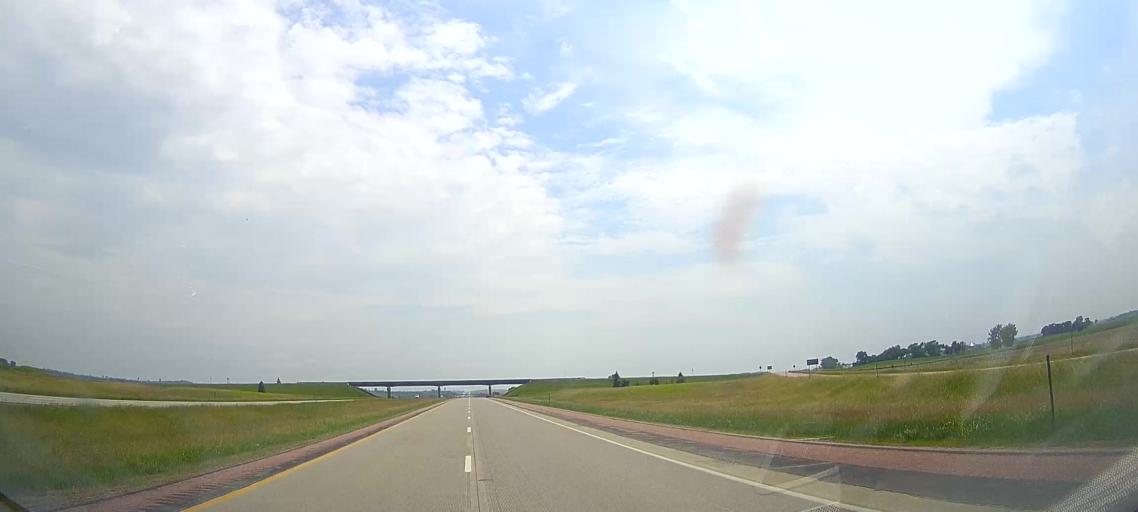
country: US
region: South Dakota
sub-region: Union County
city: Beresford
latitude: 42.9557
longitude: -96.7949
